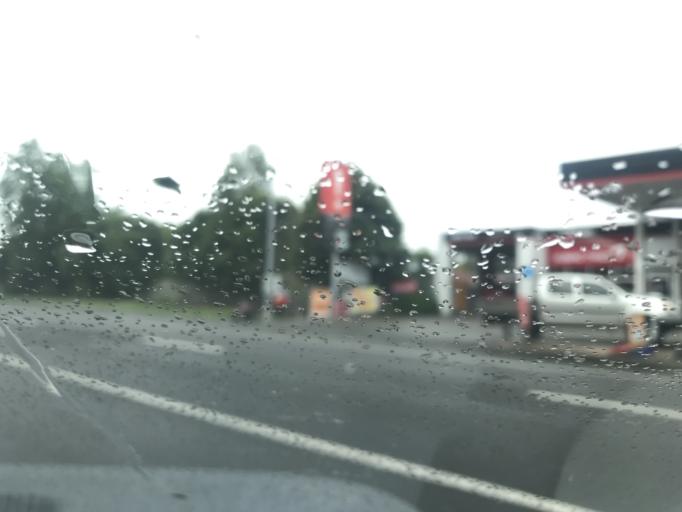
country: NZ
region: Canterbury
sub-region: Selwyn District
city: Darfield
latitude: -43.5010
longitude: 172.2167
